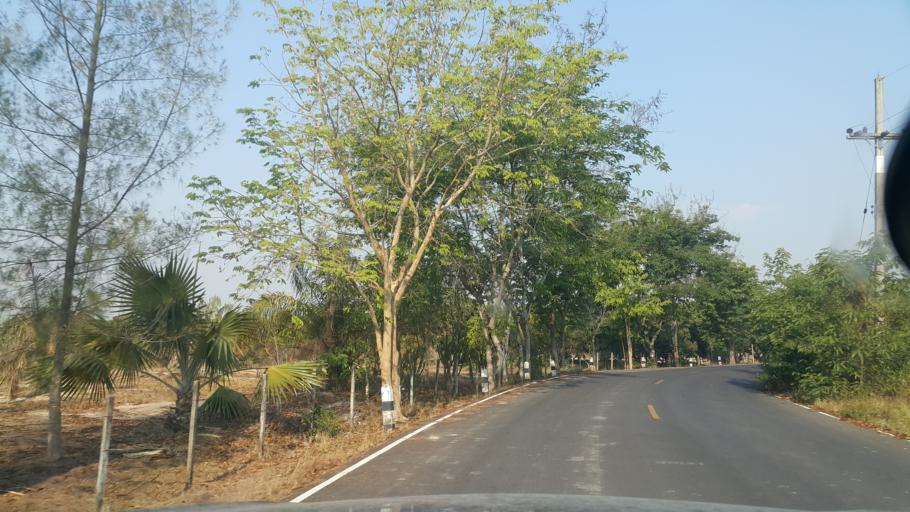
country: TH
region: Lamphun
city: Ban Thi
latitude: 18.6522
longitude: 99.0904
